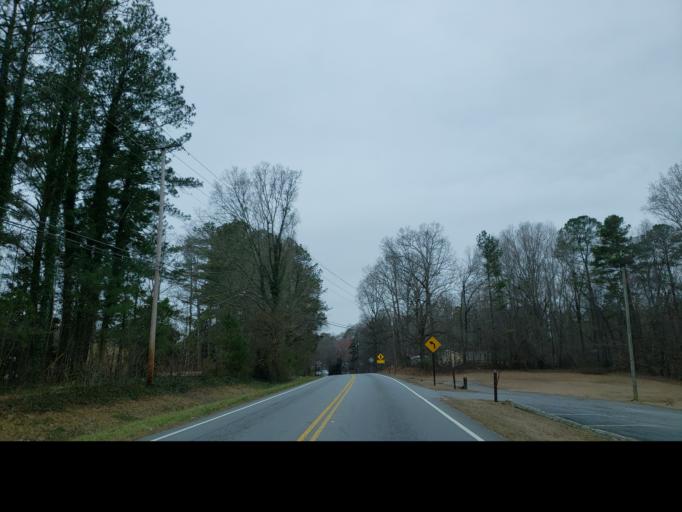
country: US
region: Georgia
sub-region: Cobb County
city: Powder Springs
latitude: 33.9239
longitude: -84.6541
